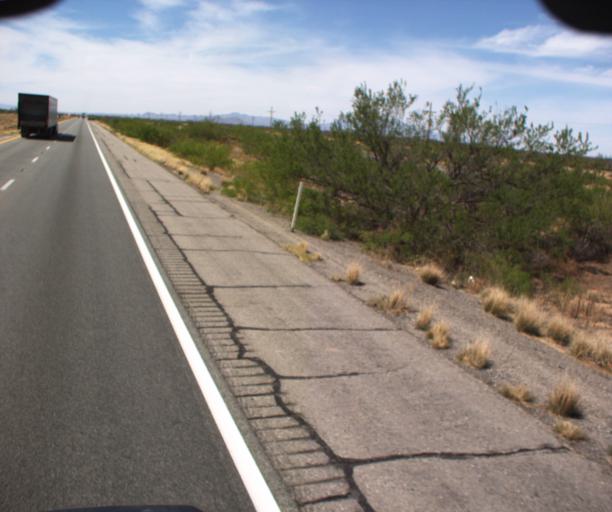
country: US
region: Arizona
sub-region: Cochise County
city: Willcox
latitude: 32.3022
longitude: -109.3745
